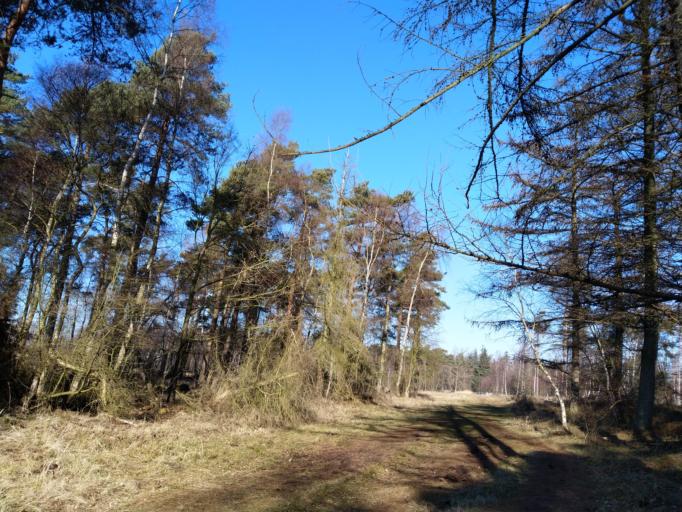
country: DK
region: Zealand
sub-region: Guldborgsund Kommune
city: Nykobing Falster
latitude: 54.6425
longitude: 11.9571
